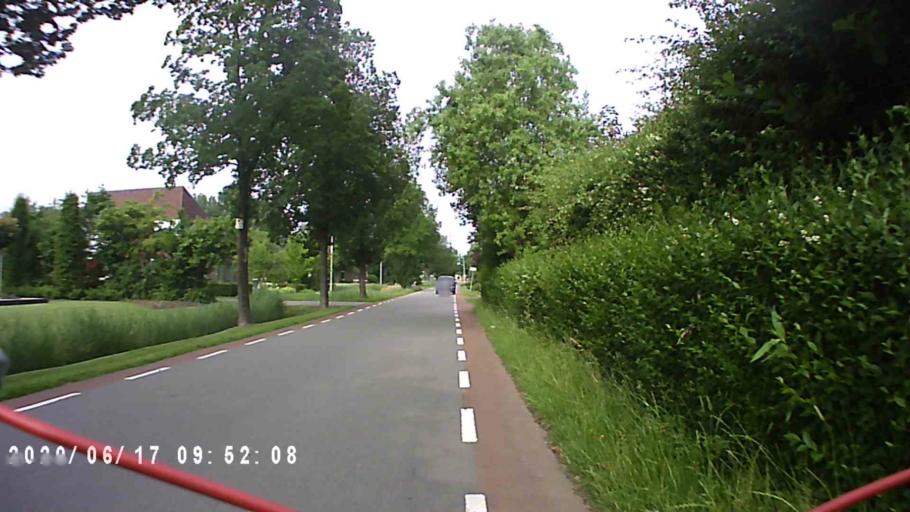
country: NL
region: Groningen
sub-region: Gemeente De Marne
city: Ulrum
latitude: 53.3596
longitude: 6.3251
